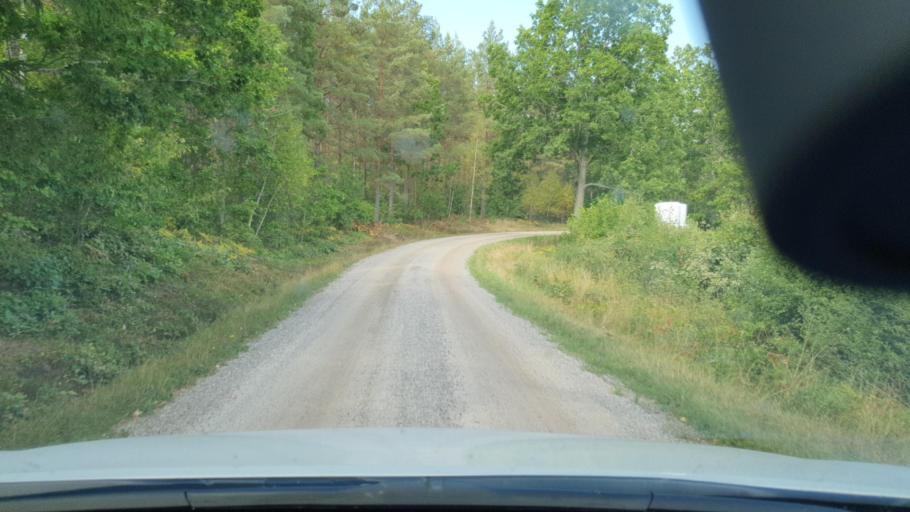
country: SE
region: Kalmar
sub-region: Vasterviks Kommun
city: Vaestervik
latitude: 57.7316
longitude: 16.4842
